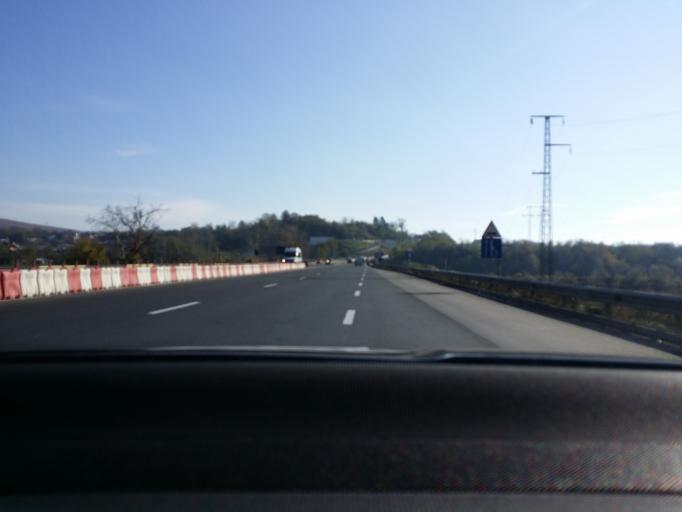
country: RO
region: Prahova
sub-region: Comuna Poiana Campina
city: Bobolia
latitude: 45.1048
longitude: 25.7500
